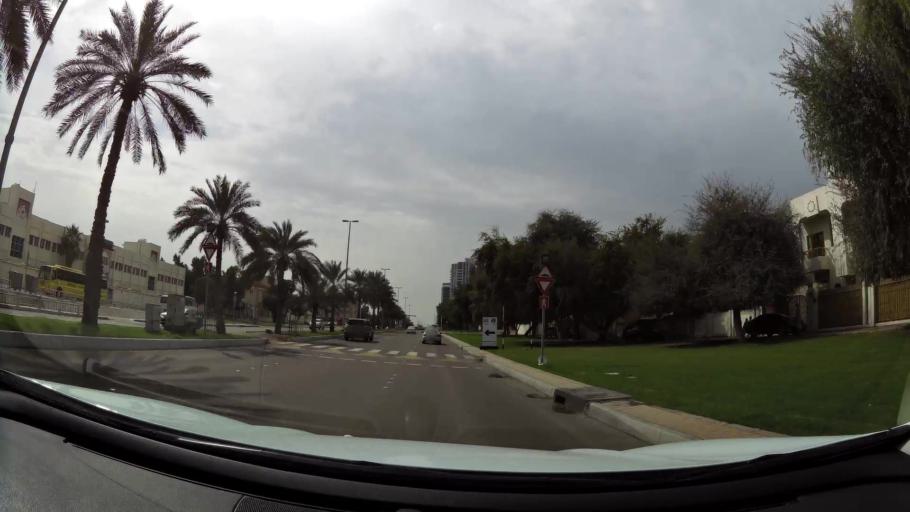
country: AE
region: Abu Dhabi
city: Abu Dhabi
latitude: 24.4364
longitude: 54.4390
